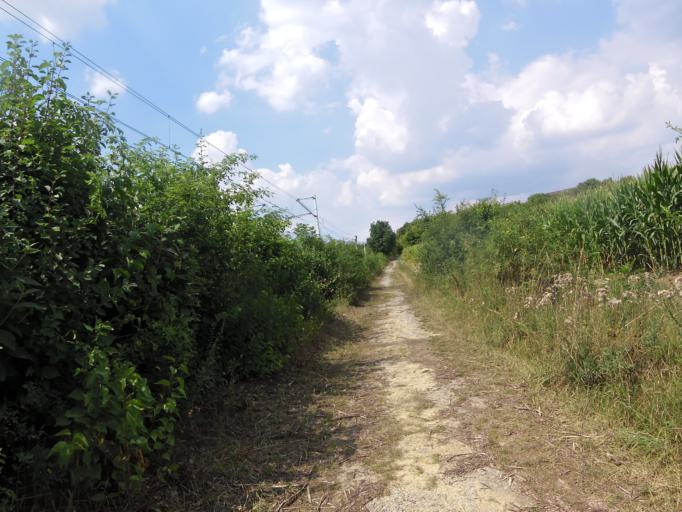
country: DE
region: Bavaria
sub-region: Regierungsbezirk Unterfranken
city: Randersacker
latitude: 49.7351
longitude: 9.9632
